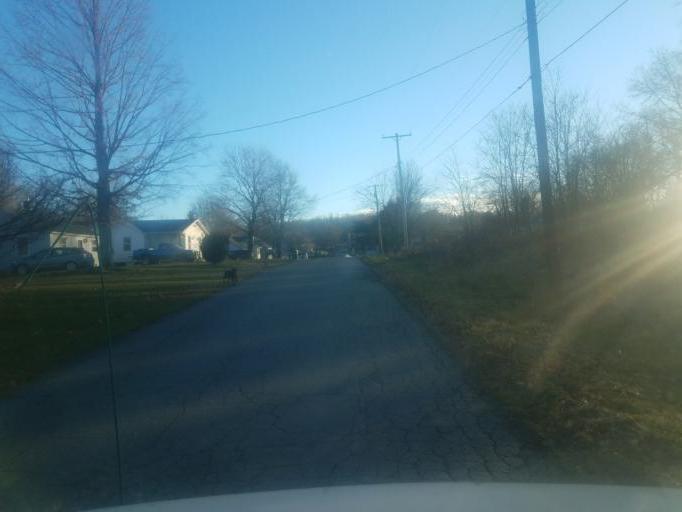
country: US
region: Ohio
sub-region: Richland County
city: Mansfield
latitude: 40.7890
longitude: -82.5449
